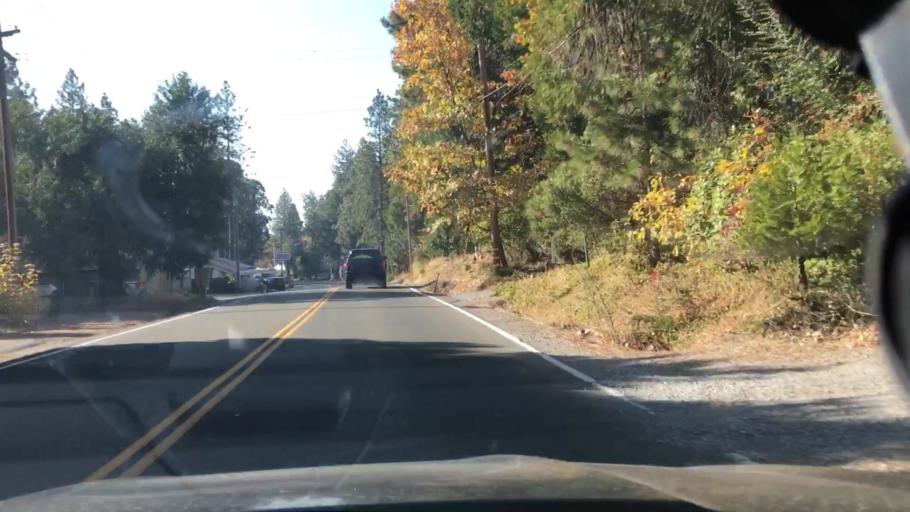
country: US
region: California
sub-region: El Dorado County
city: Camino
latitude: 38.7446
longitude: -120.6548
